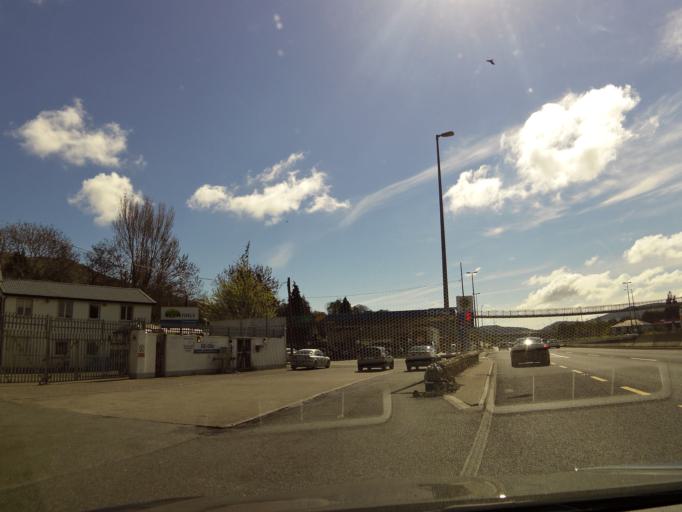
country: IE
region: Leinster
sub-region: Wicklow
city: Kilmacanoge
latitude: 53.1705
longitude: -6.1360
